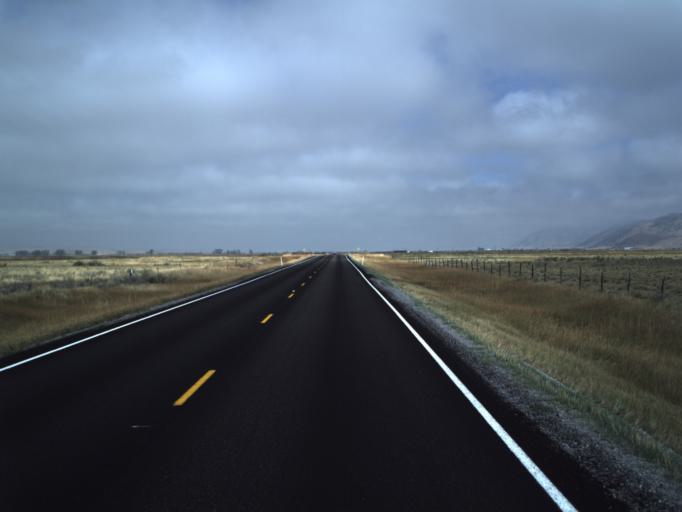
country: US
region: Utah
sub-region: Rich County
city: Randolph
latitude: 41.4929
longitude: -111.1200
